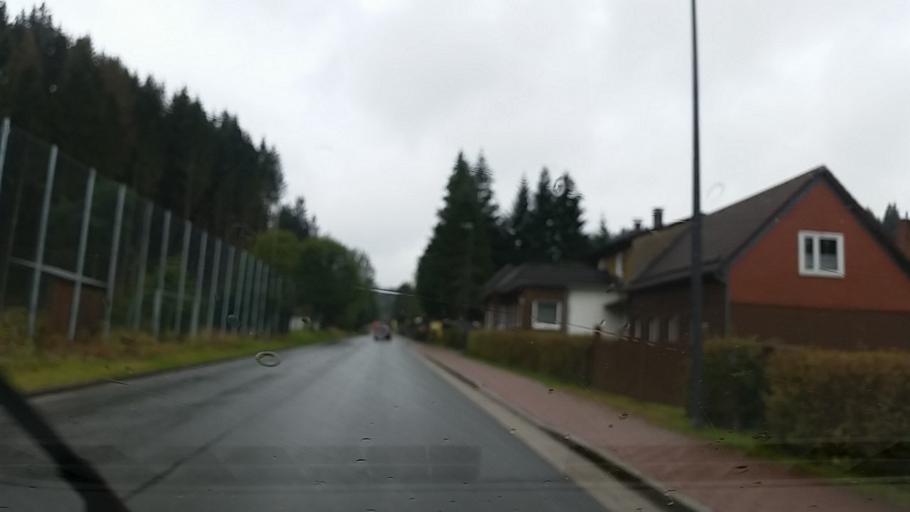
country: DE
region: Lower Saxony
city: Altenau
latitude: 51.8125
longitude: 10.4377
